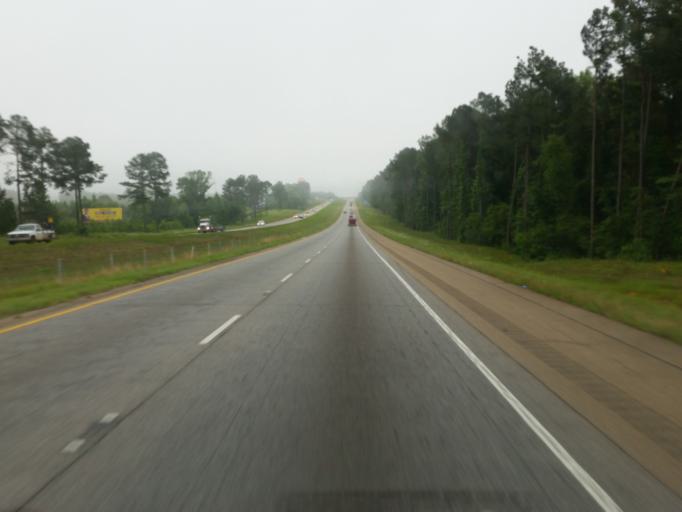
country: US
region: Louisiana
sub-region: Webster Parish
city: Minden
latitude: 32.5834
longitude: -93.2628
